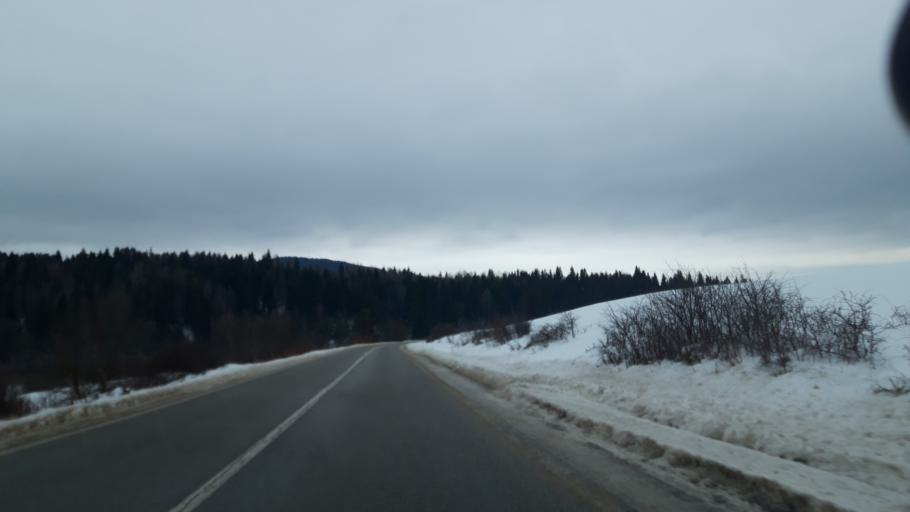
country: BA
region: Republika Srpska
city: Han Pijesak
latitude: 44.0057
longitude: 18.8908
